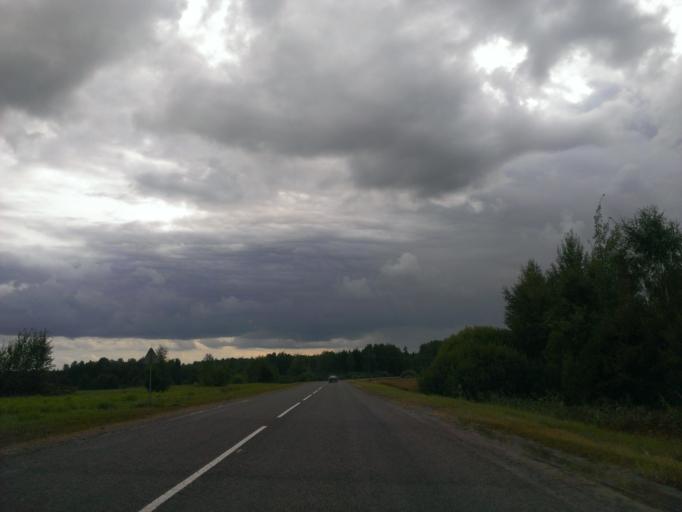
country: LV
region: Kegums
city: Kegums
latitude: 56.7697
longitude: 24.7695
